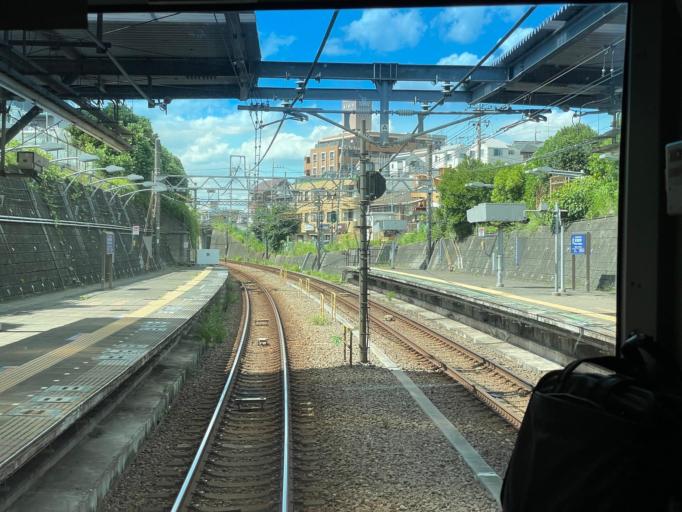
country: JP
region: Kanagawa
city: Minami-rinkan
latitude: 35.4530
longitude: 139.5263
